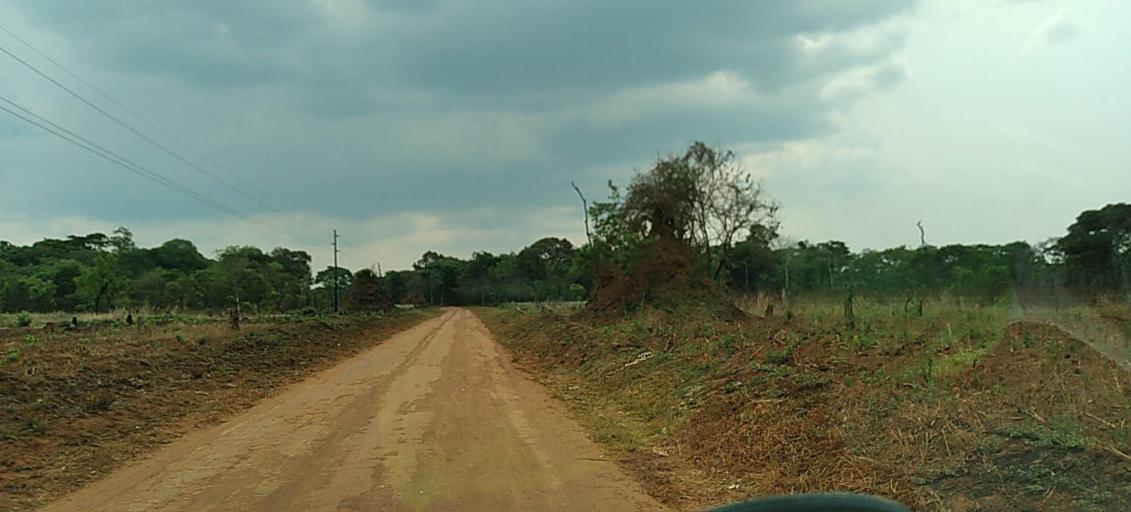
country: ZM
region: North-Western
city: Solwezi
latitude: -12.7817
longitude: 26.4942
